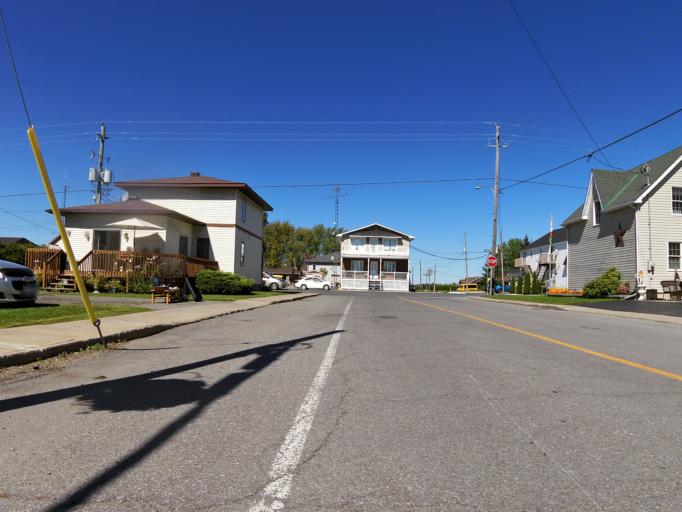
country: CA
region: Ontario
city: Casselman
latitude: 45.2547
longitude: -75.1219
